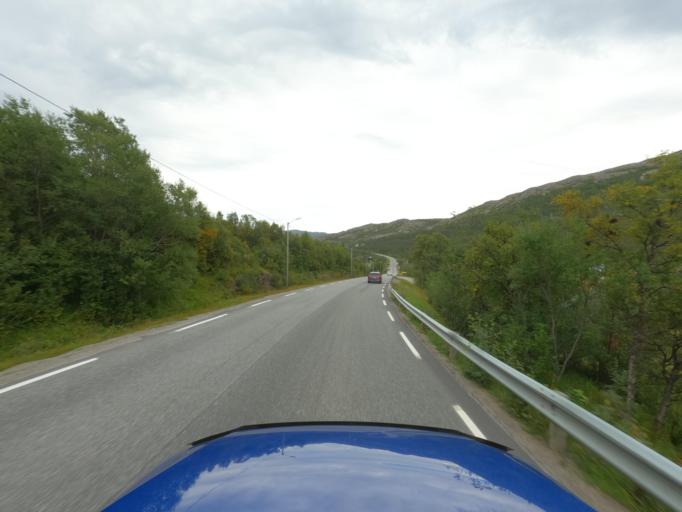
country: NO
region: Finnmark Fylke
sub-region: Kvalsund
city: Kvalsund
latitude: 70.4802
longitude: 24.2069
